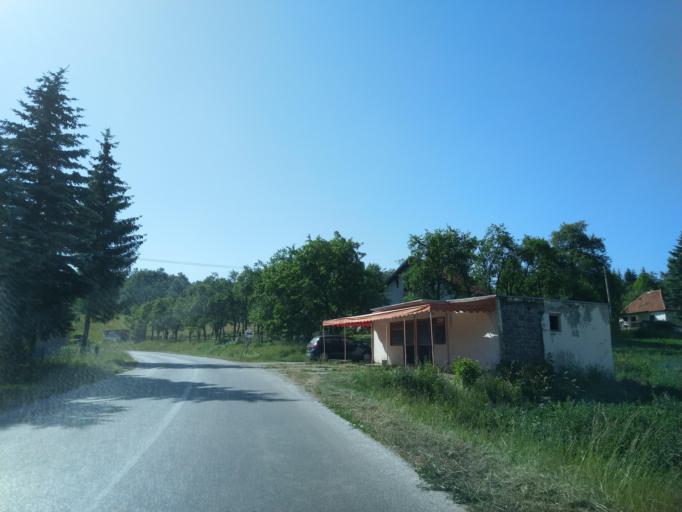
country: RS
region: Central Serbia
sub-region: Zlatiborski Okrug
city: Uzice
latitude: 43.8801
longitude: 19.7475
